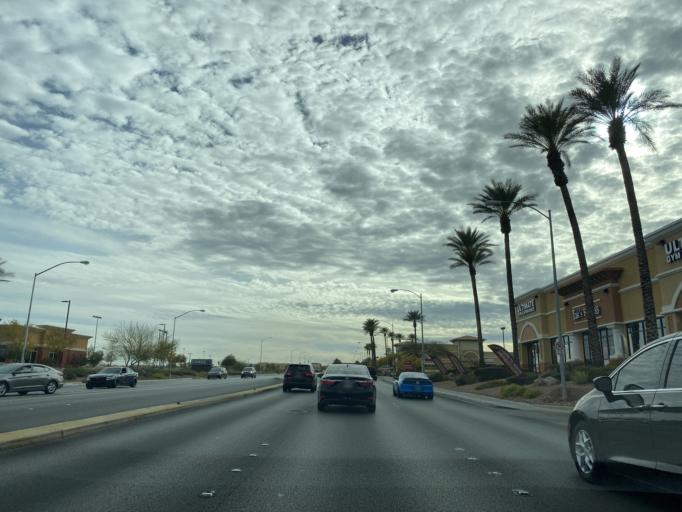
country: US
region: Nevada
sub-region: Clark County
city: Enterprise
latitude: 36.0550
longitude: -115.2793
